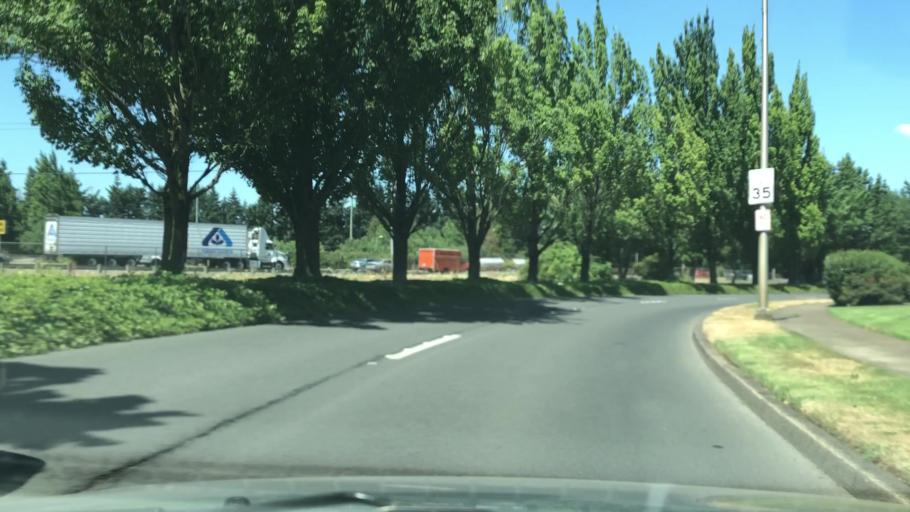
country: US
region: Oregon
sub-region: Clackamas County
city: Wilsonville
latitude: 45.3056
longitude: -122.7681
